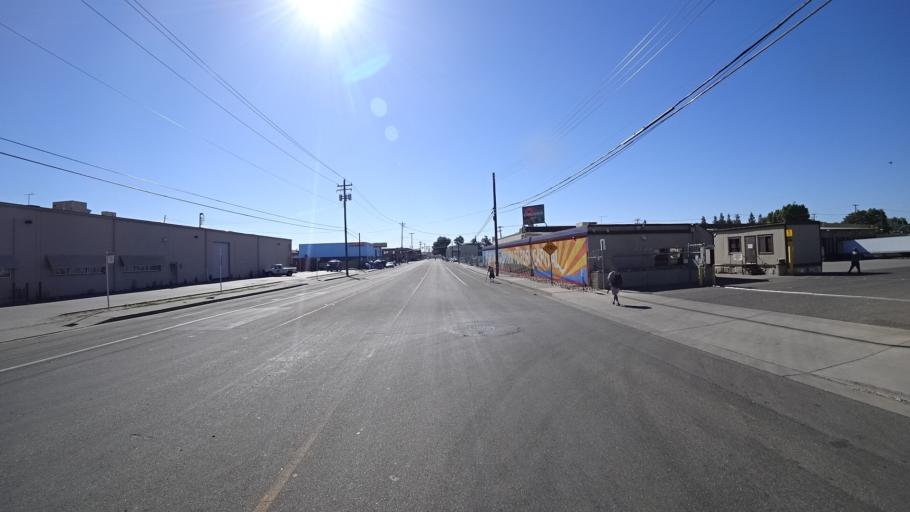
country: US
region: California
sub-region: Sacramento County
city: Sacramento
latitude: 38.5901
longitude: -121.4846
